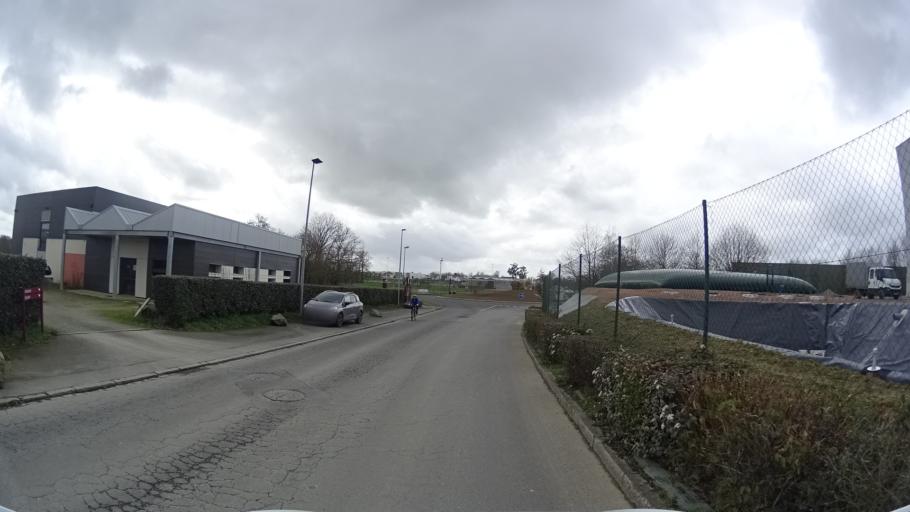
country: FR
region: Brittany
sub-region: Departement d'Ille-et-Vilaine
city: Saint-Gilles
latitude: 48.1574
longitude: -1.8333
